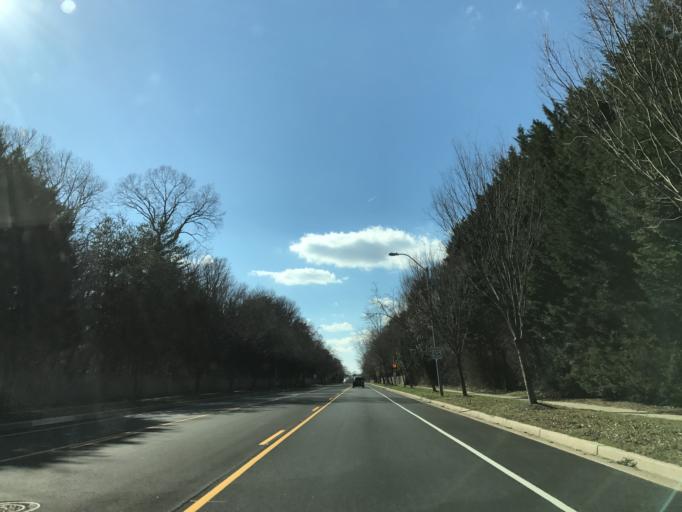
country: US
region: Maryland
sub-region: Anne Arundel County
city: South Gate
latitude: 39.1063
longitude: -76.6090
